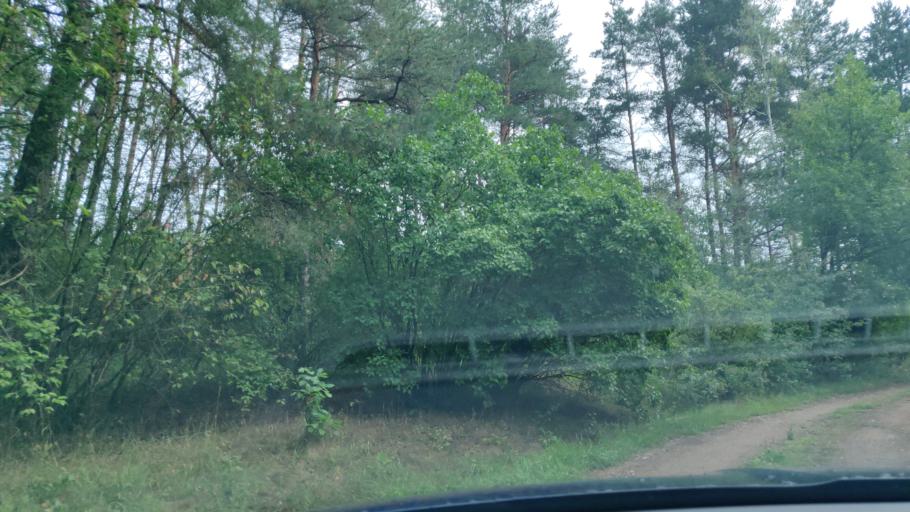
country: LT
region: Vilnius County
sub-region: Trakai
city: Rudiskes
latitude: 54.6100
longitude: 24.8264
